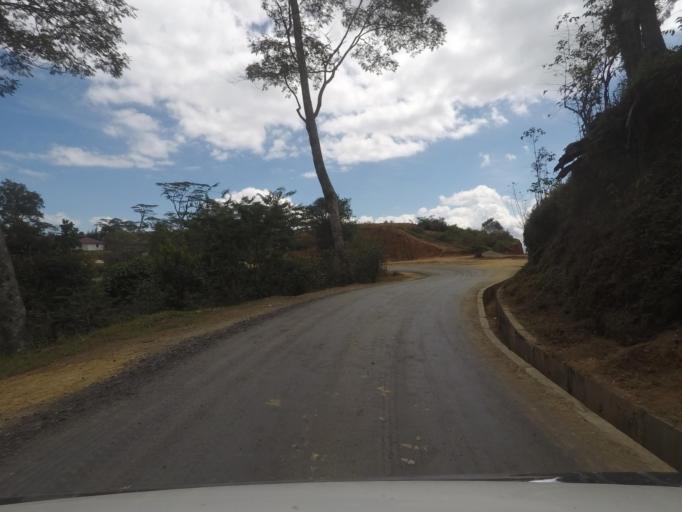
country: TL
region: Ermera
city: Gleno
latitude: -8.7501
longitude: 125.3545
